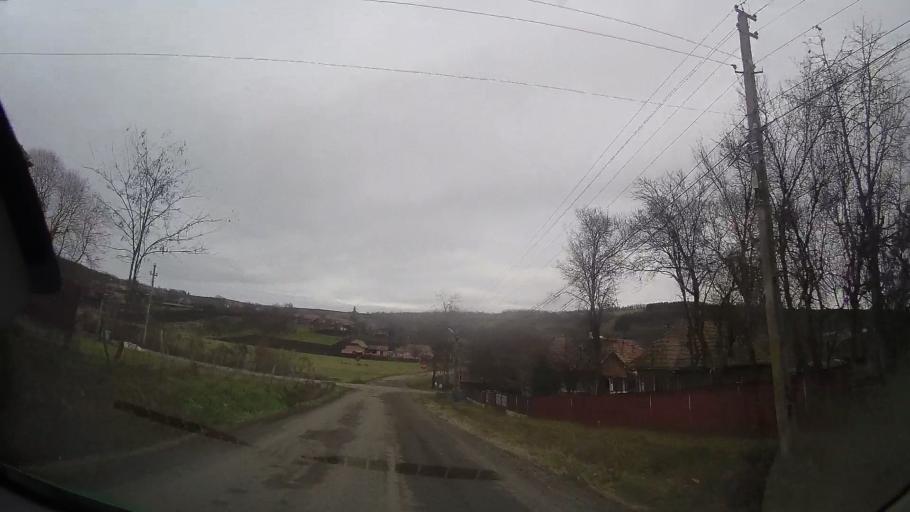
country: RO
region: Mures
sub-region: Comuna Bala
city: Bala
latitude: 46.7078
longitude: 24.5015
